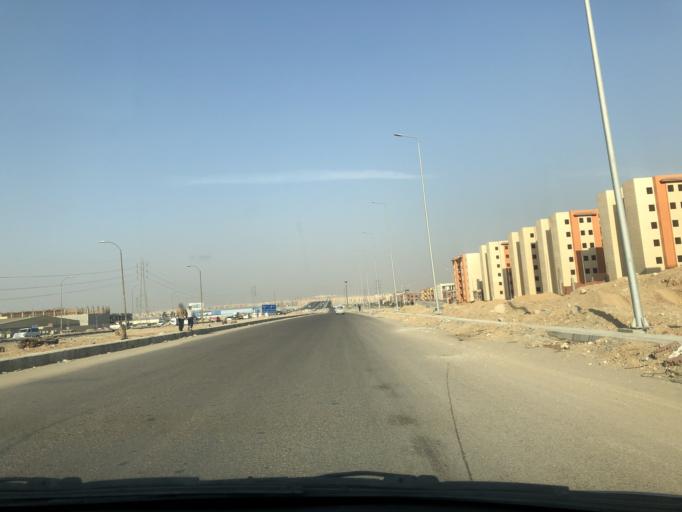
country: EG
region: Al Jizah
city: Madinat Sittah Uktubar
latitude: 29.9051
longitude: 30.9190
